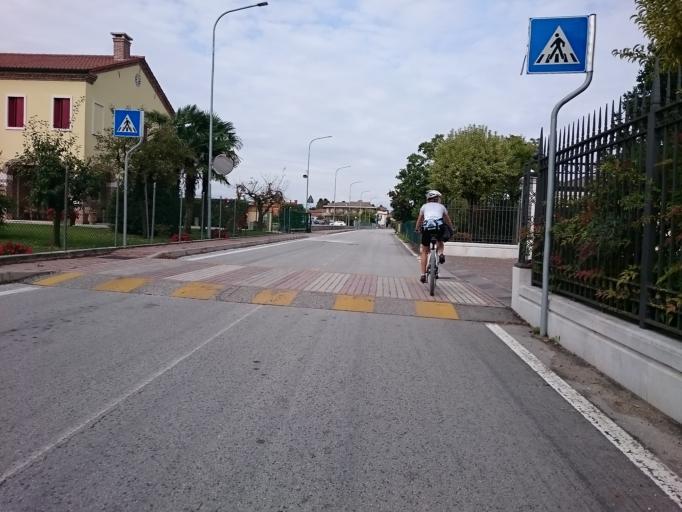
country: IT
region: Veneto
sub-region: Provincia di Padova
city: San Pietro in Gu
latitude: 45.5805
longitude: 11.6638
